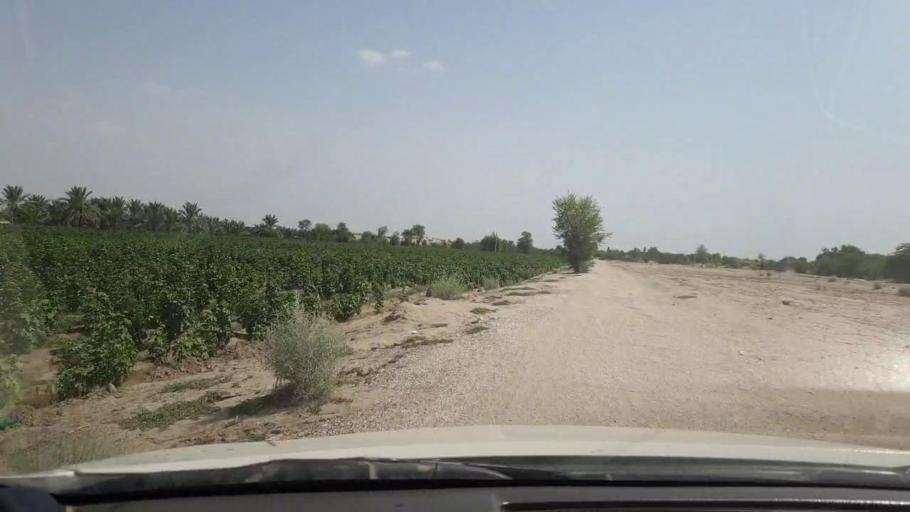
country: PK
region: Sindh
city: Rohri
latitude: 27.4689
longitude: 69.0790
